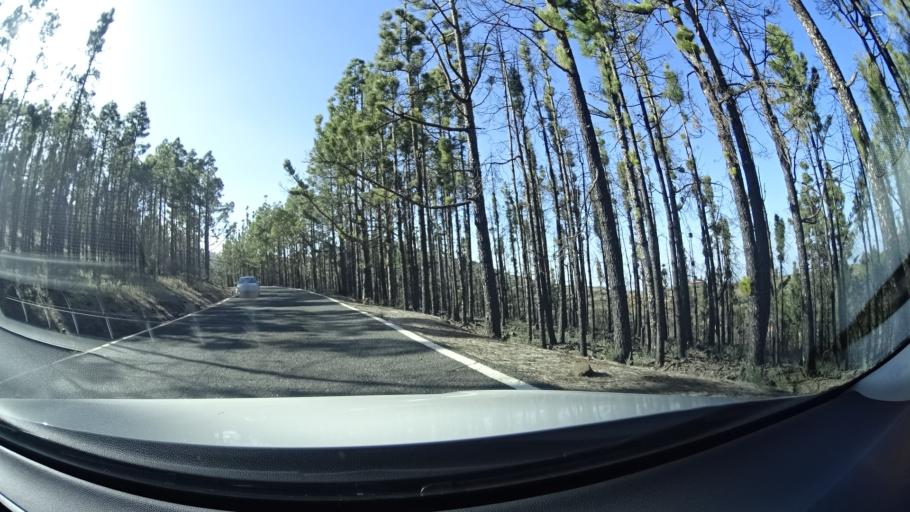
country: ES
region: Canary Islands
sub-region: Provincia de Las Palmas
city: San Bartolome
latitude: 27.9647
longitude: -15.5532
